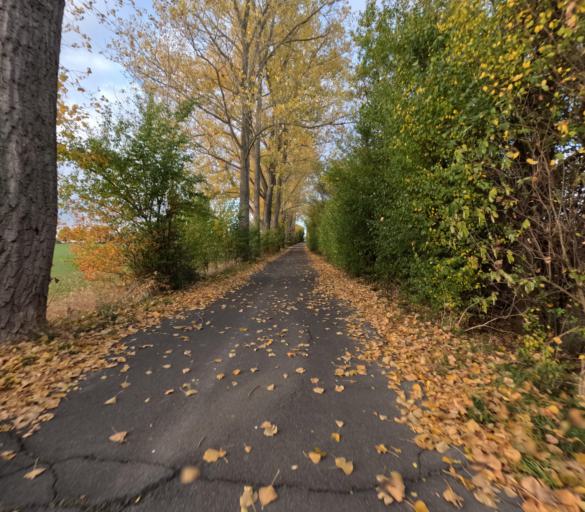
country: DE
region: Saxony
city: Grimma
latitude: 51.2507
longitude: 12.6948
